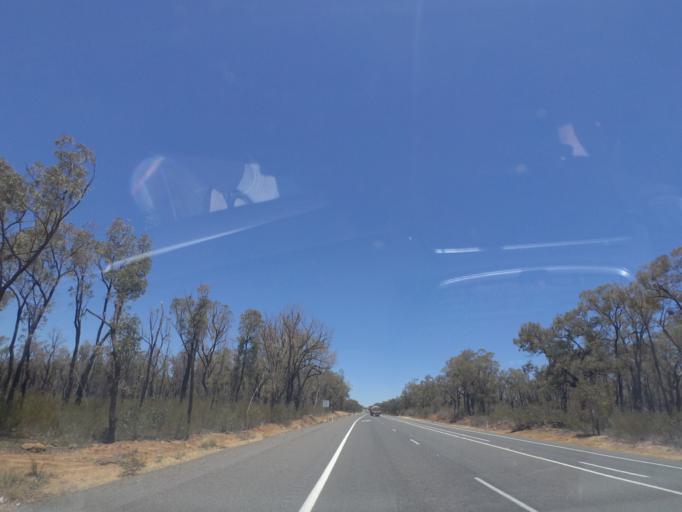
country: AU
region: New South Wales
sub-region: Warrumbungle Shire
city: Coonabarabran
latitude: -30.9043
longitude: 149.4383
